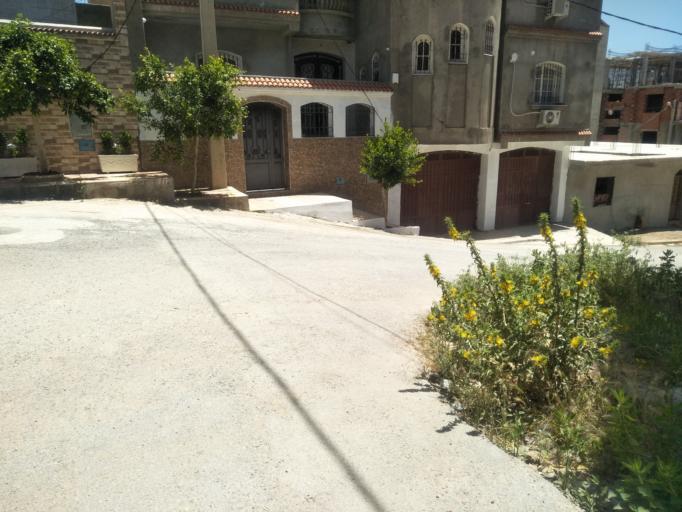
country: DZ
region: Tlemcen
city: Mansoura
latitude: 34.8737
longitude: -1.3677
